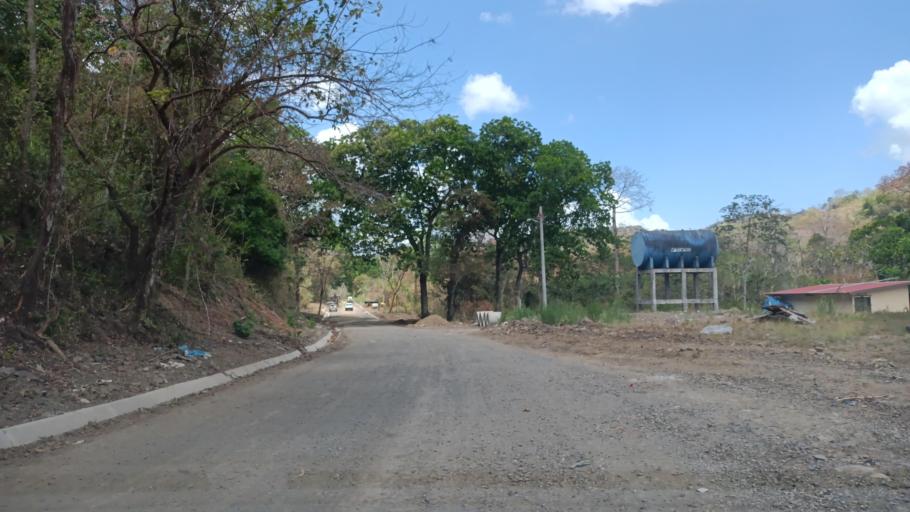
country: PA
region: Panama
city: Las Cumbres
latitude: 9.0645
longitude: -79.5666
